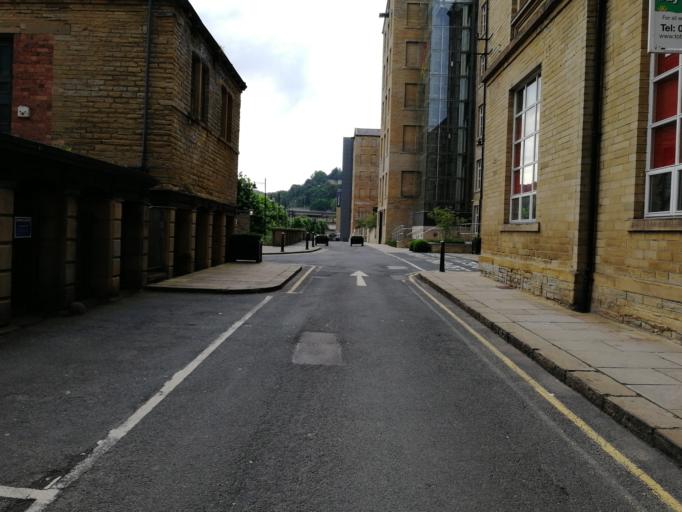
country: GB
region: England
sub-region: Calderdale
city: Halifax
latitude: 53.7287
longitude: -1.8645
